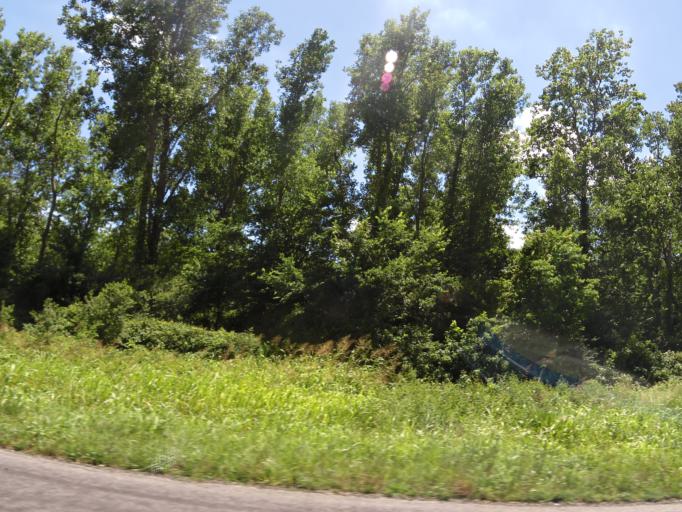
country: US
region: Missouri
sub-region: Pemiscot County
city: Caruthersville
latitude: 36.1414
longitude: -89.6408
